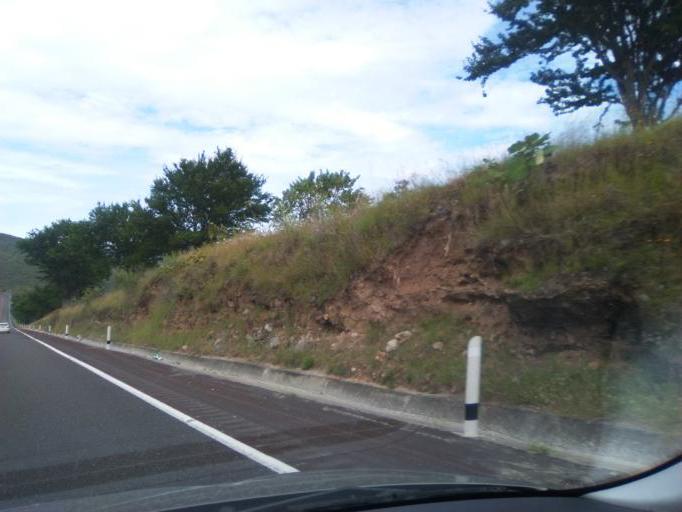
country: MX
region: Guerrero
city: Huitziltepec
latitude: 17.7562
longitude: -99.4886
